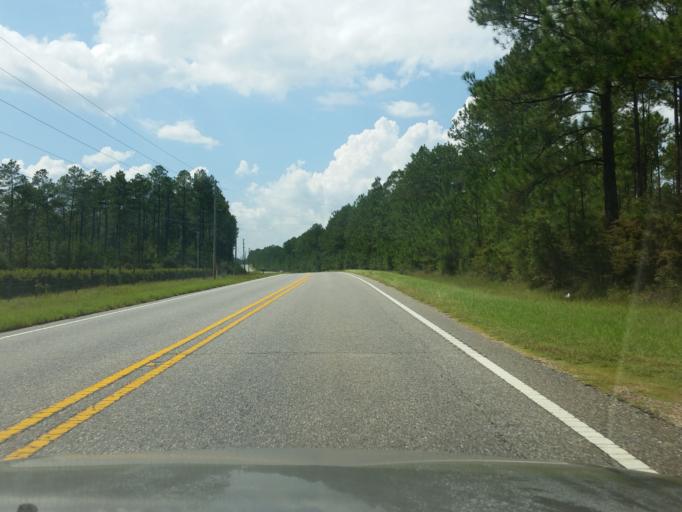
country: US
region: Alabama
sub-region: Baldwin County
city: Elberta
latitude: 30.5241
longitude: -87.4972
